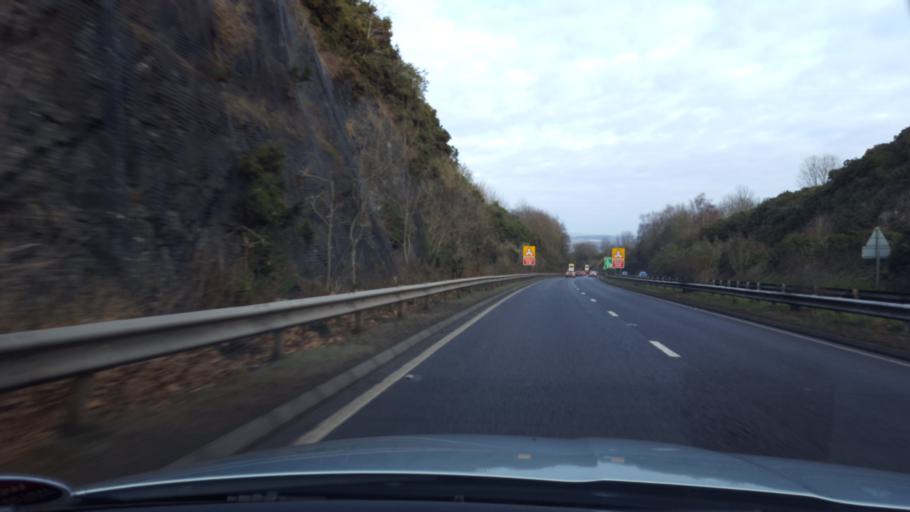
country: GB
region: Scotland
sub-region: Fife
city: Newport-On-Tay
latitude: 56.4419
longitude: -2.9326
